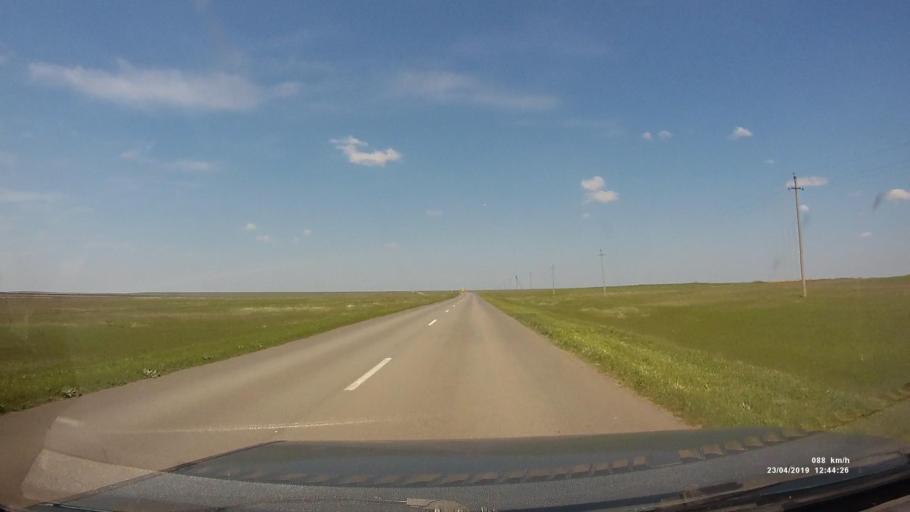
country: RU
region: Kalmykiya
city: Yashalta
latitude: 46.4768
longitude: 42.6474
